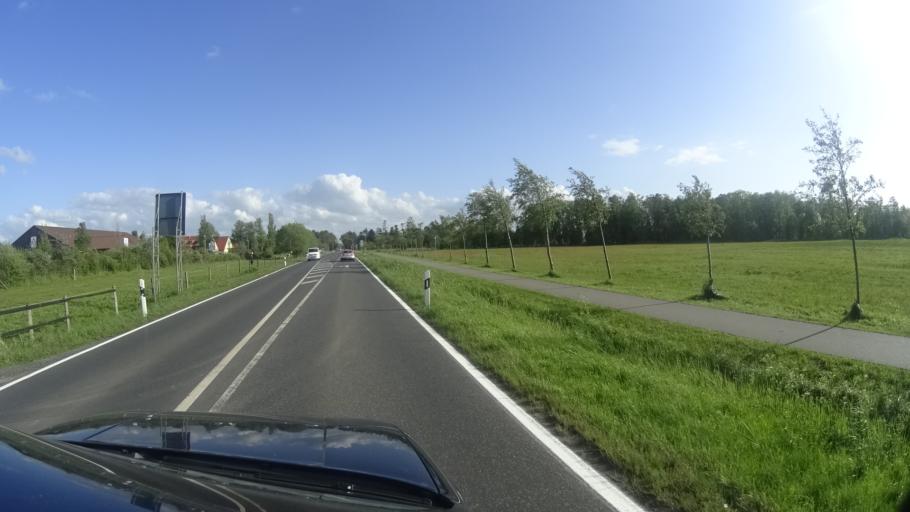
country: DE
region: Mecklenburg-Vorpommern
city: Ostseebad Dierhagen
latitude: 54.2943
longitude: 12.3519
